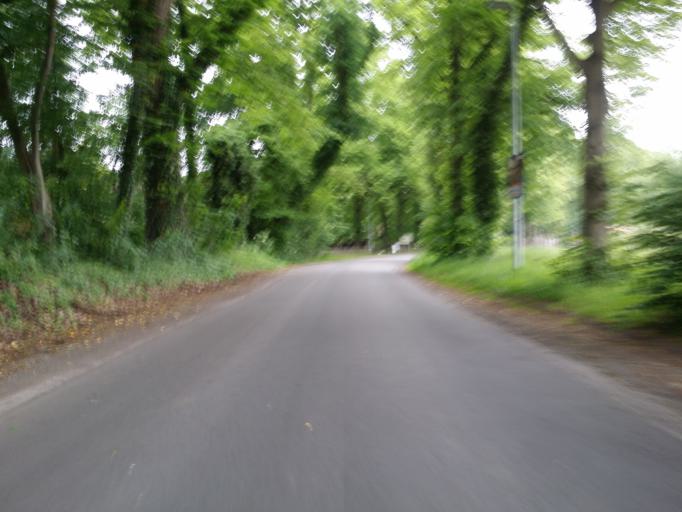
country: DE
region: Lower Saxony
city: Rastede
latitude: 53.2270
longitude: 8.2554
